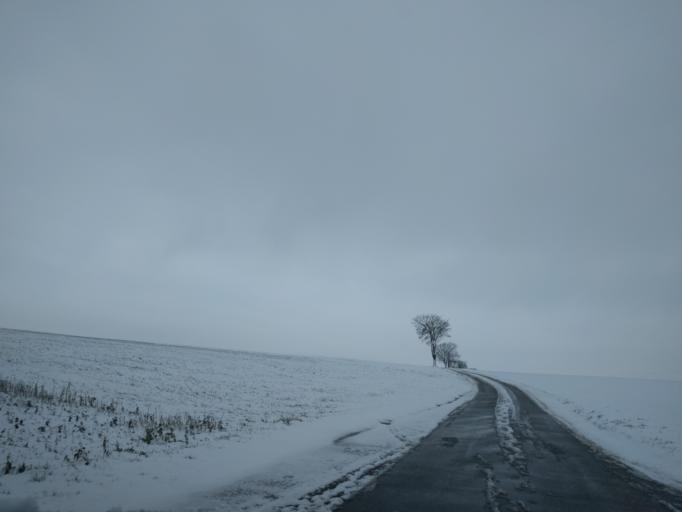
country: DE
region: Bavaria
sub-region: Swabia
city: Donauwoerth
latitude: 48.7021
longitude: 10.7349
